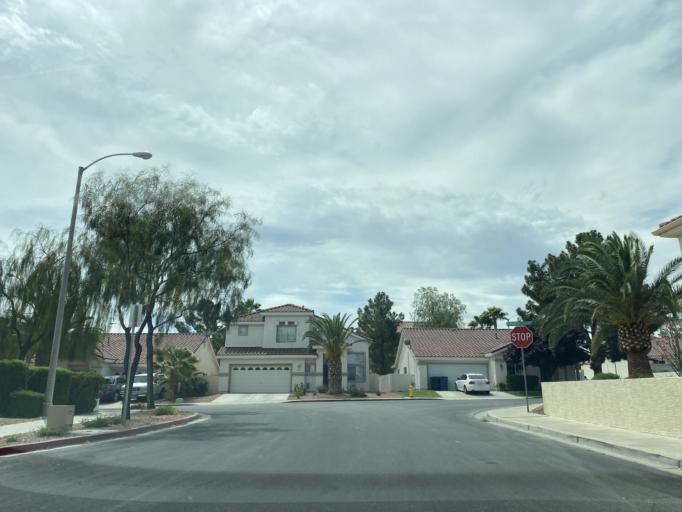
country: US
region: Nevada
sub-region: Clark County
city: Whitney
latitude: 36.0249
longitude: -115.0678
